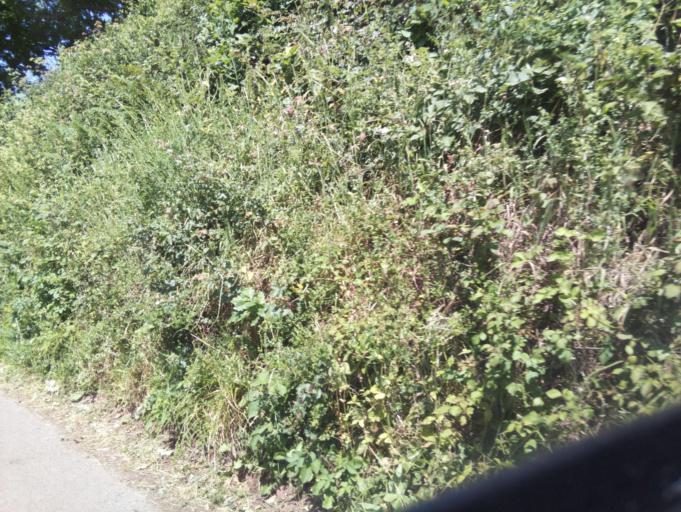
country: GB
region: England
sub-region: Devon
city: Marldon
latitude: 50.4640
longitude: -3.5957
